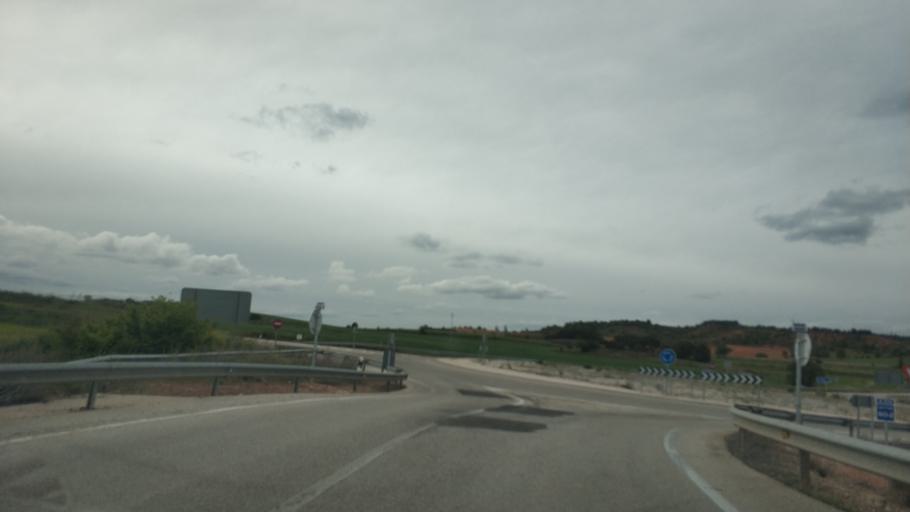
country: ES
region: Castille and Leon
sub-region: Provincia de Soria
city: El Burgo de Osma
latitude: 41.5851
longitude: -3.0418
